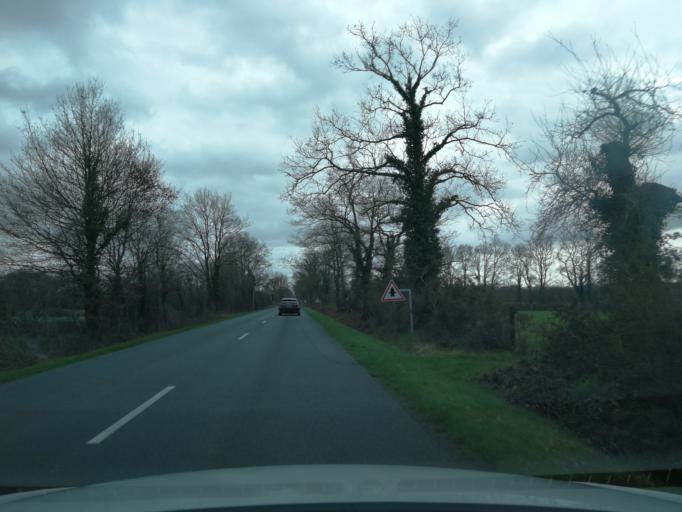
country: FR
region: Pays de la Loire
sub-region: Departement de la Loire-Atlantique
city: Montbert
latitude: 47.0197
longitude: -1.4881
